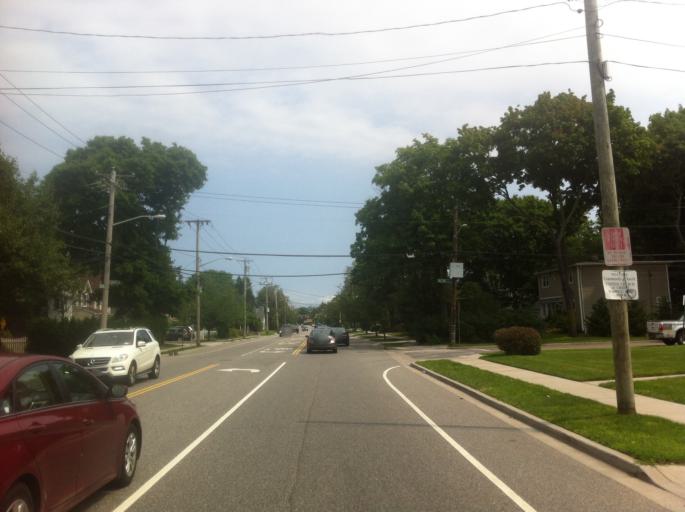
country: US
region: New York
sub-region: Nassau County
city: Syosset
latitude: 40.8115
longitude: -73.5016
